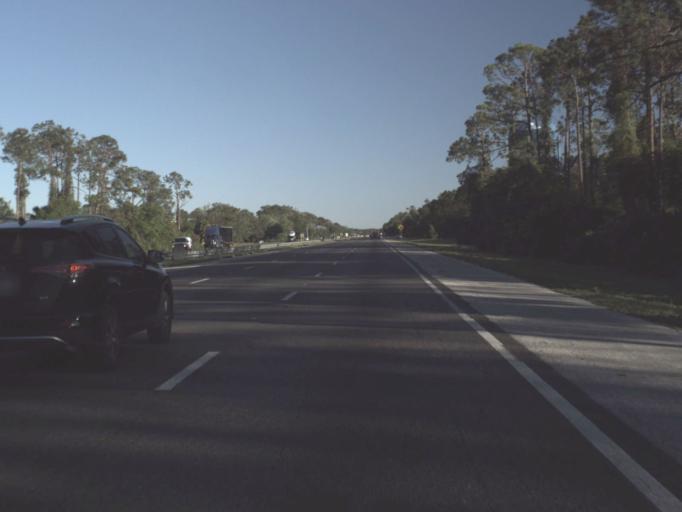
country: US
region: Florida
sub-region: Flagler County
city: Palm Coast
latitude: 29.5531
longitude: -81.2184
